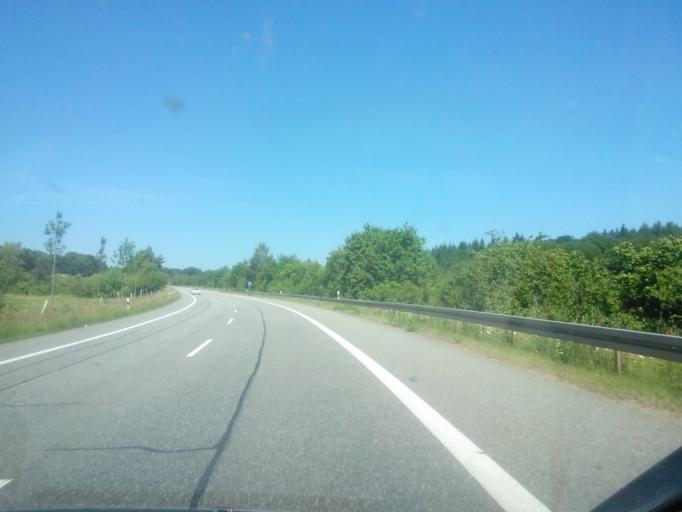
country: DE
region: Saarland
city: Losheim
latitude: 49.5065
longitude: 6.7901
